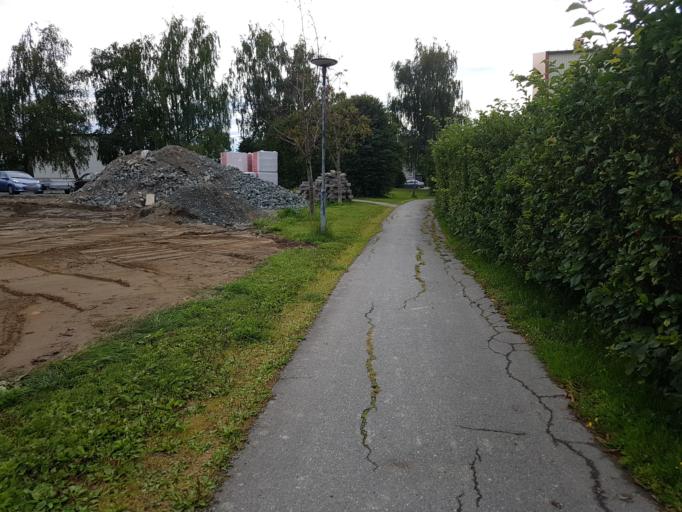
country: NO
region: Sor-Trondelag
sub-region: Trondheim
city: Trondheim
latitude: 63.4039
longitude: 10.4160
